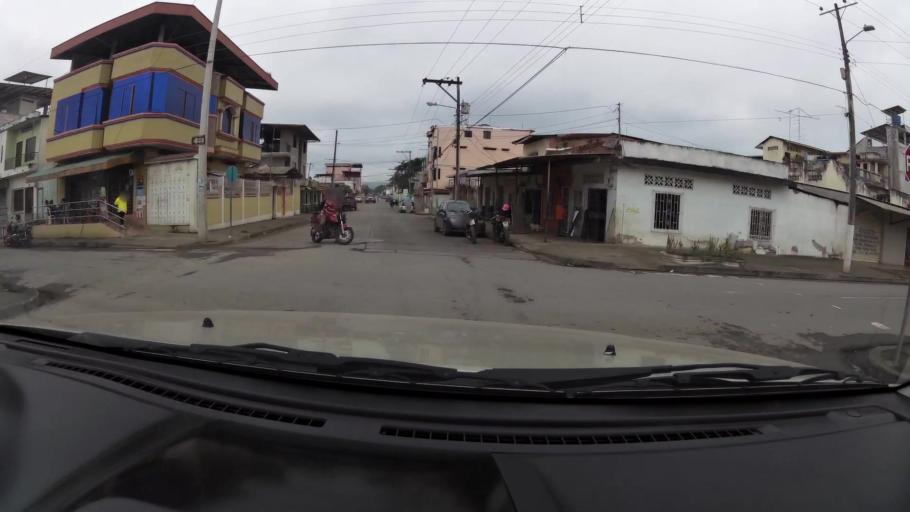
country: EC
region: El Oro
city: Pasaje
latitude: -3.3318
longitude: -79.8090
